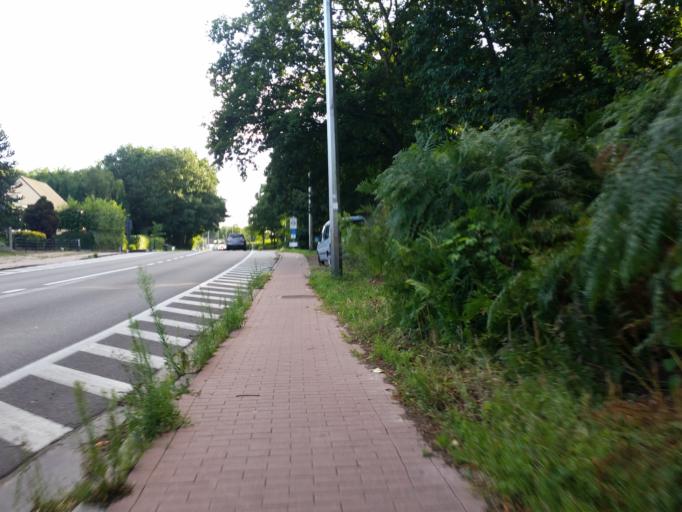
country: BE
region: Flanders
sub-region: Provincie Antwerpen
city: Duffel
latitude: 51.0804
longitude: 4.4956
